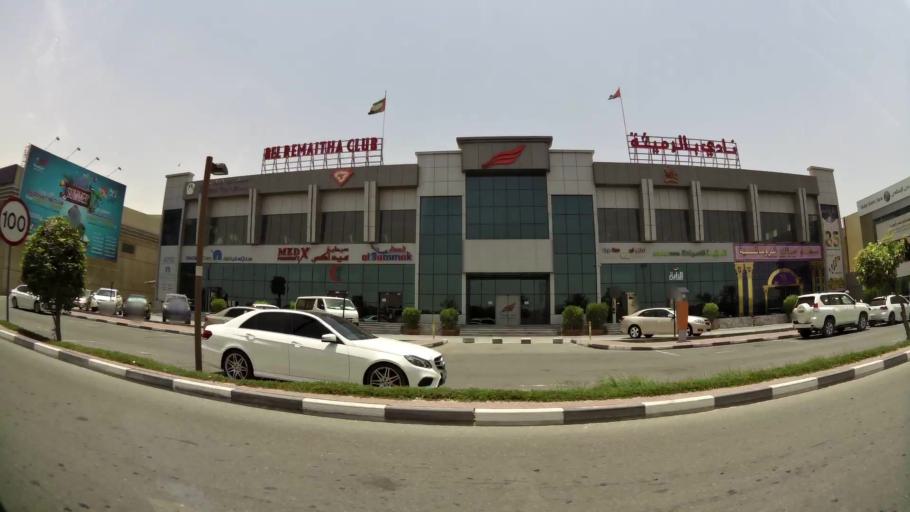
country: AE
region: Ash Shariqah
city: Sharjah
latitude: 25.2140
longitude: 55.3797
